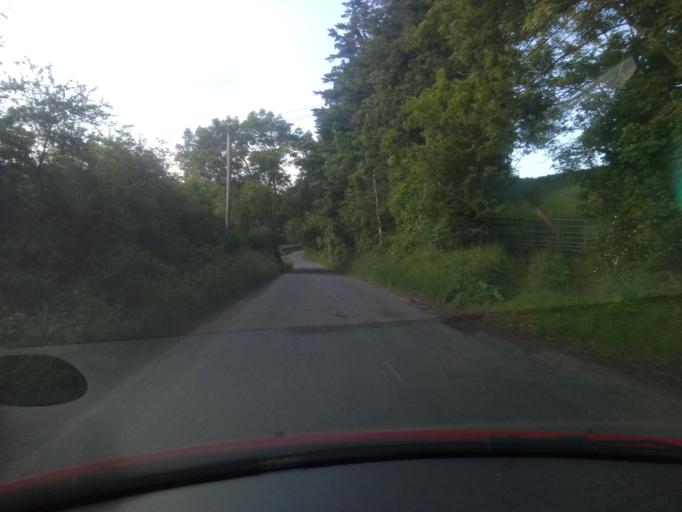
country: GB
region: Scotland
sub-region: The Scottish Borders
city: Selkirk
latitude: 55.5187
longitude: -2.9238
